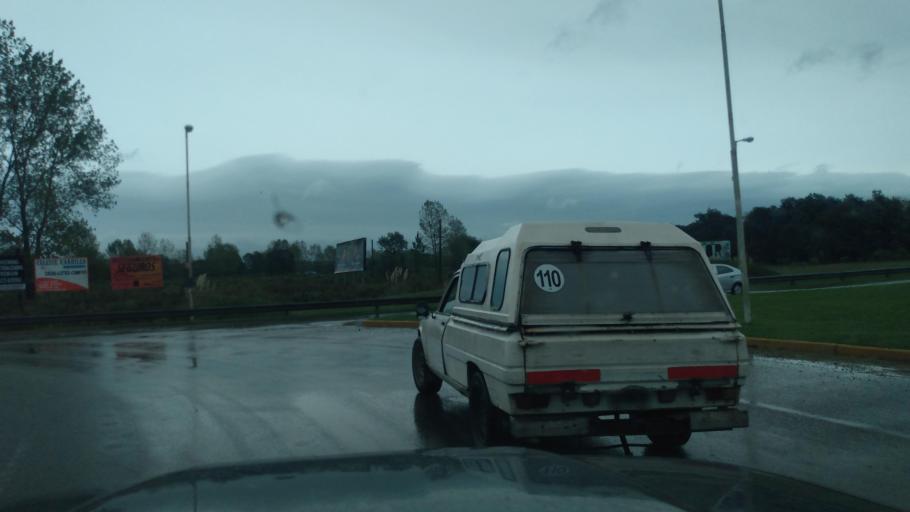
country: AR
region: Buenos Aires
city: Capilla del Senor
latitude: -34.3893
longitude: -59.0356
